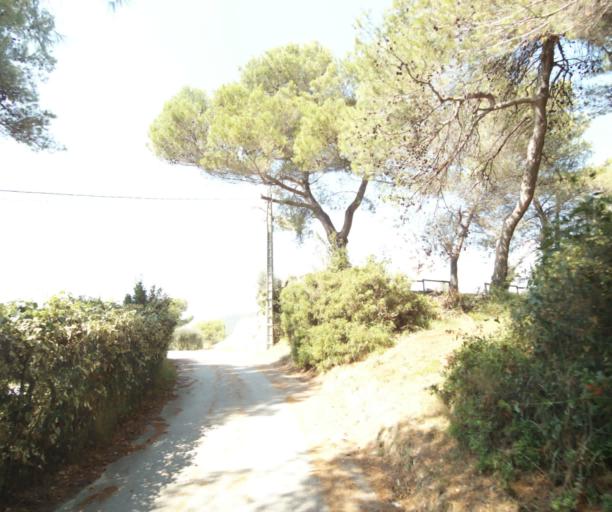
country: FR
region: Provence-Alpes-Cote d'Azur
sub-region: Departement des Alpes-Maritimes
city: Drap
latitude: 43.7595
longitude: 7.3300
